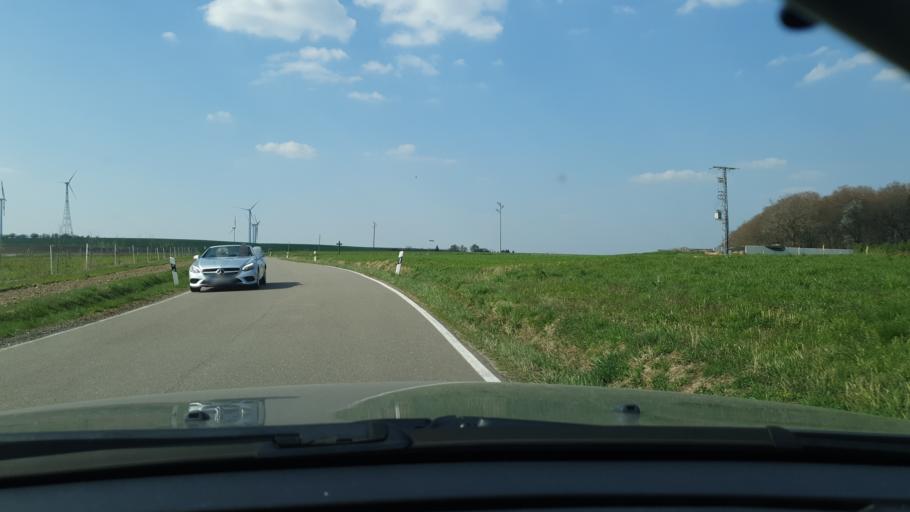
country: DE
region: Rheinland-Pfalz
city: Knopp-Labach
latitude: 49.3247
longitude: 7.5027
